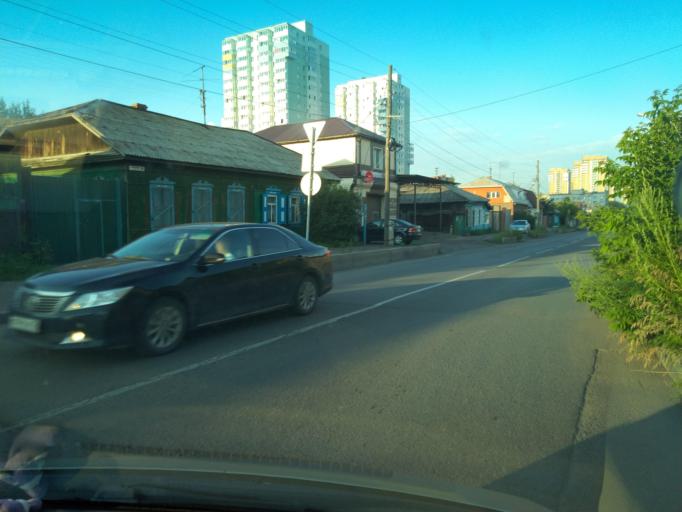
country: RU
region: Krasnoyarskiy
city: Krasnoyarsk
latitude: 56.0311
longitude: 92.8995
